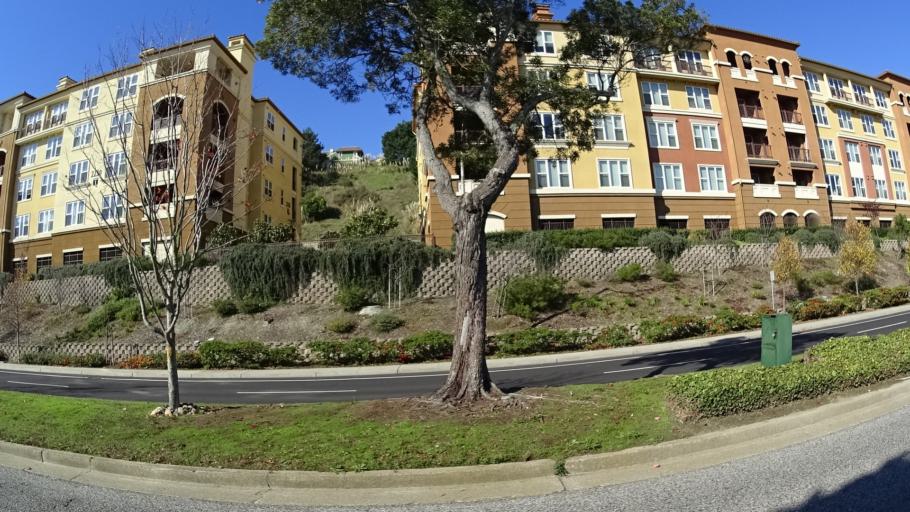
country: US
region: California
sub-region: San Mateo County
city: Colma
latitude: 37.6462
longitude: -122.4534
